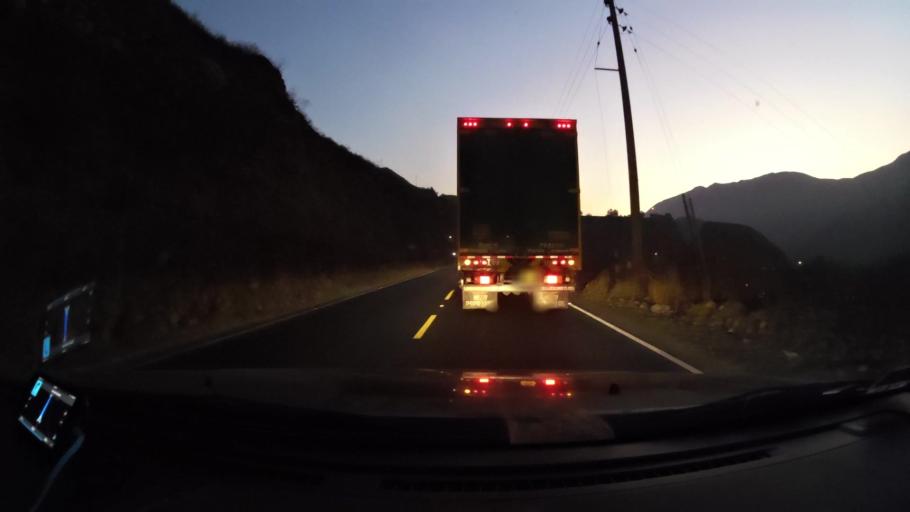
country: PE
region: Lima
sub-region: Provincia de Huarochiri
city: Cocachacra
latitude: -11.9057
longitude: -76.5205
